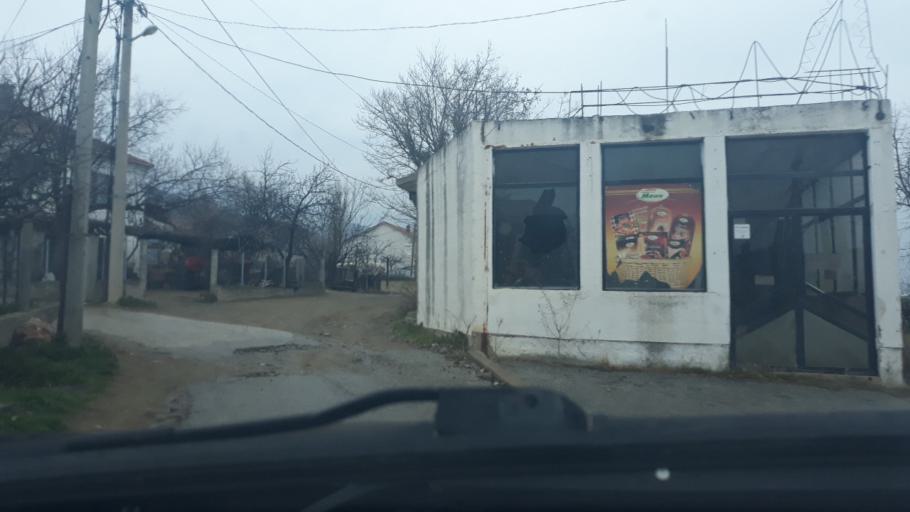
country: MK
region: Dojran
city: Star Dojran
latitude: 41.2630
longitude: 22.7483
